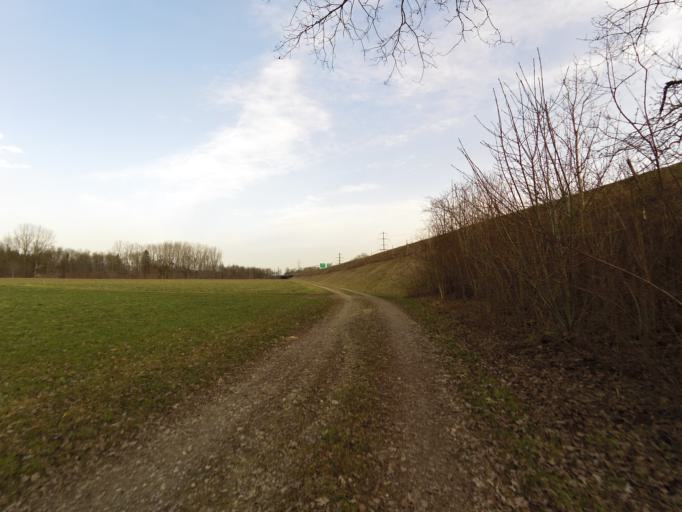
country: CH
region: Thurgau
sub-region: Frauenfeld District
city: Mullheim
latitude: 47.5884
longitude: 8.9855
